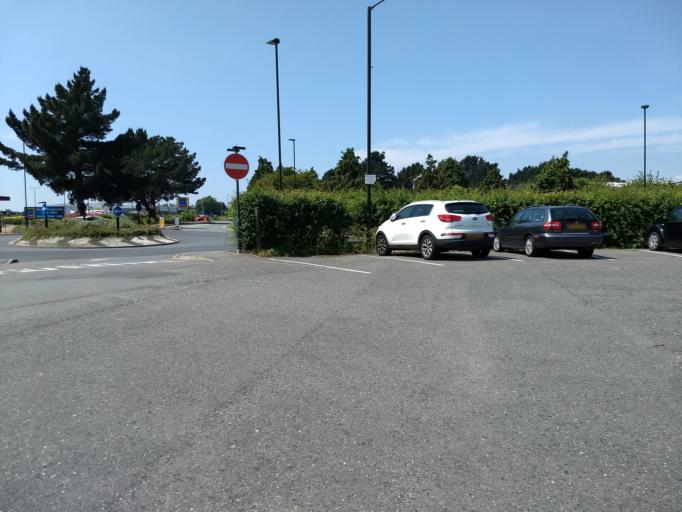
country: GB
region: England
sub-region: Isle of Wight
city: Northwood
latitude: 50.7499
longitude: -1.3045
